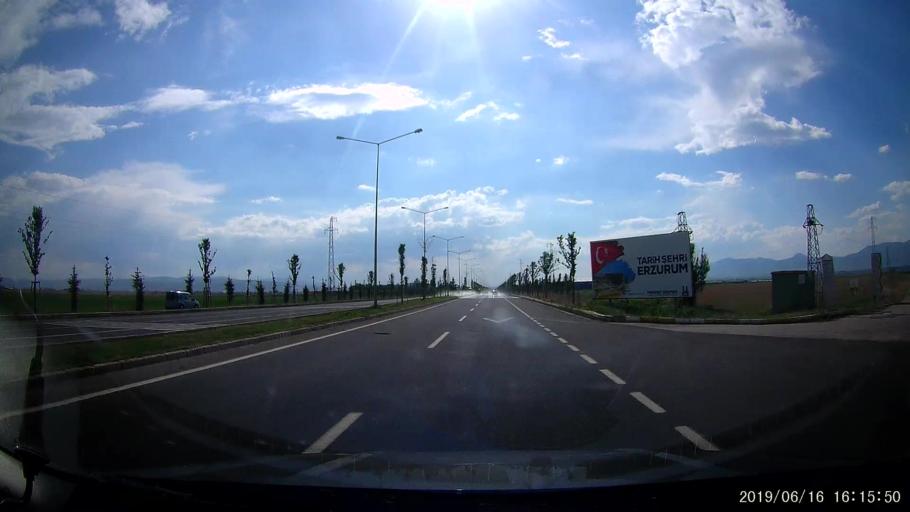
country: TR
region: Erzurum
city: Erzurum
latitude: 39.9623
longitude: 41.2180
